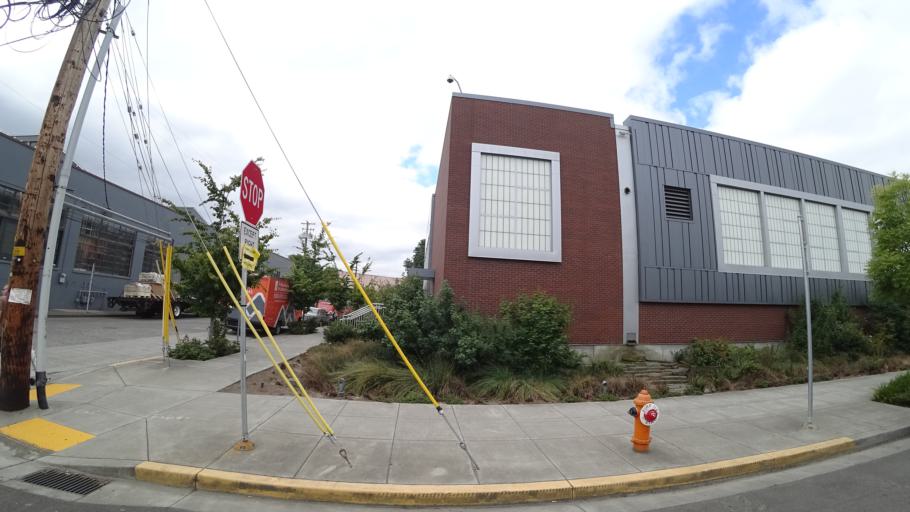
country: US
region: Oregon
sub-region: Multnomah County
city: Portland
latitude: 45.5378
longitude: -122.6719
